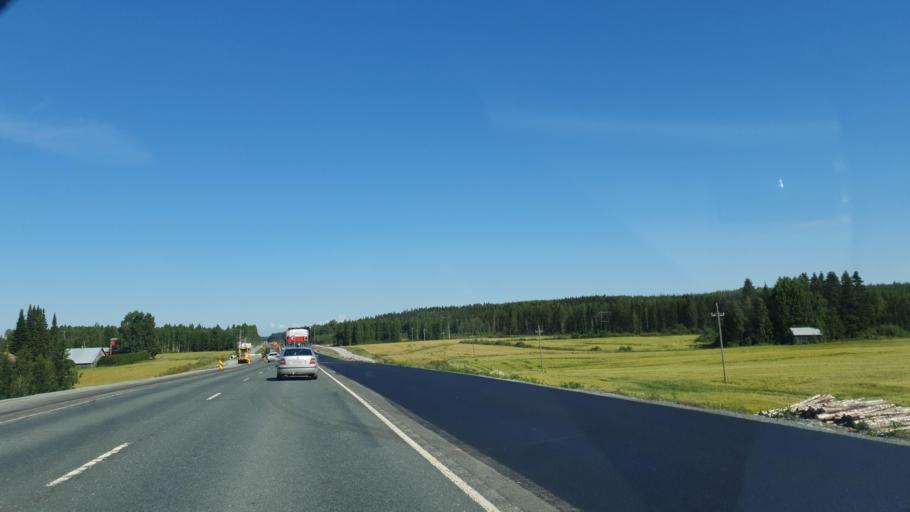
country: FI
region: Northern Savo
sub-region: Ylae-Savo
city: Lapinlahti
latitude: 63.2850
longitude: 27.4552
